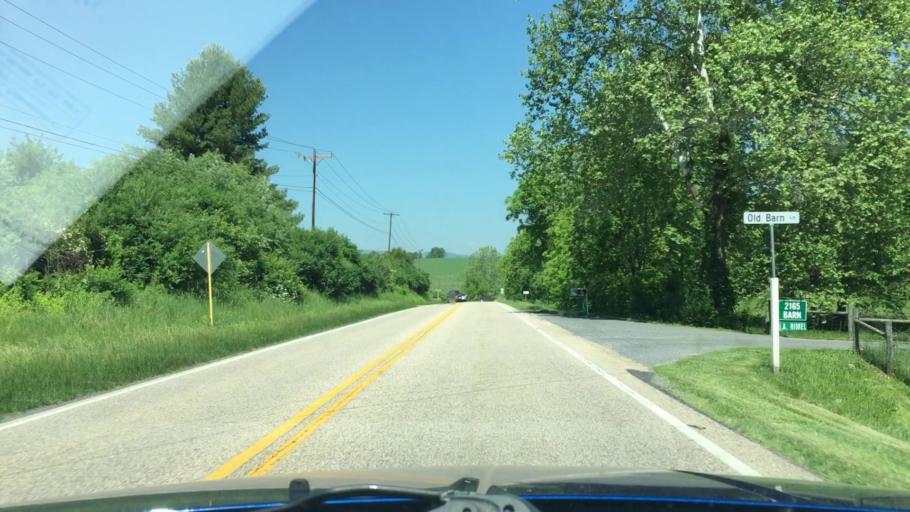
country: US
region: Virginia
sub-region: City of Staunton
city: Staunton
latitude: 38.1904
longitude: -79.1083
